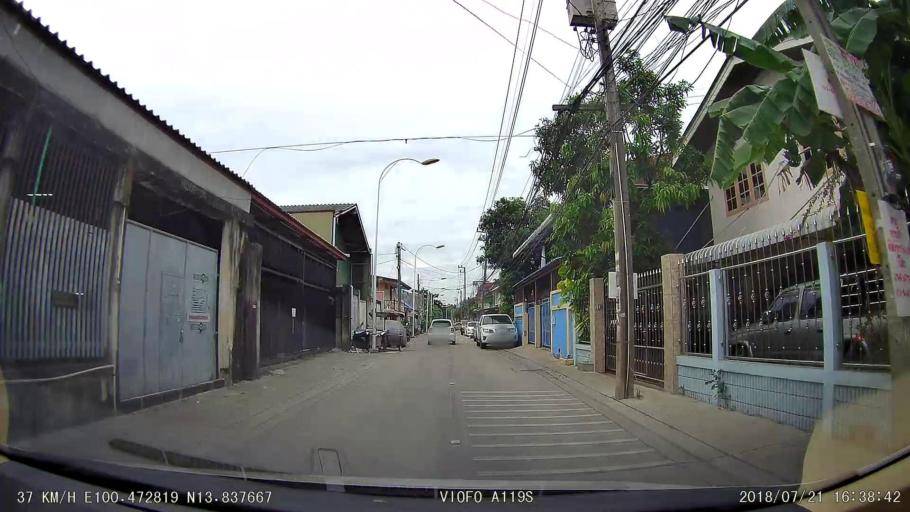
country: TH
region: Nonthaburi
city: Bang Kruai
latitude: 13.8378
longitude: 100.4727
